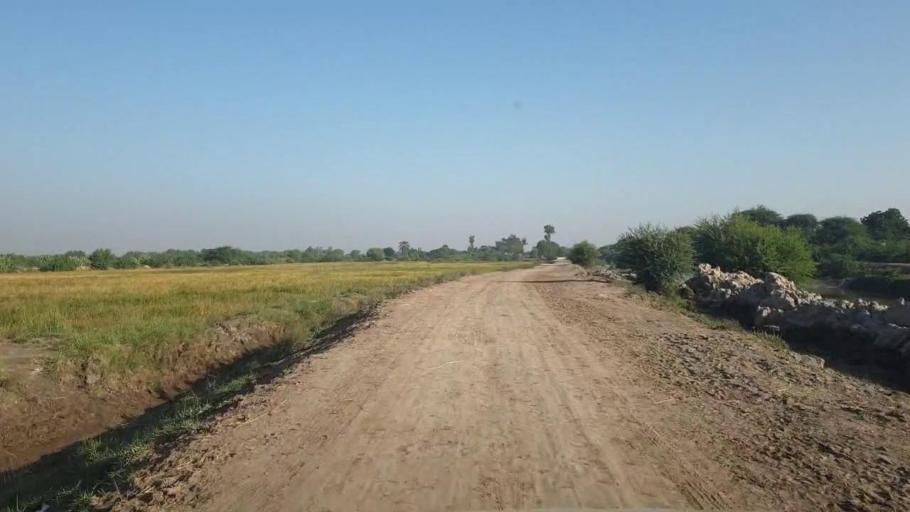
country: PK
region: Sindh
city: Badin
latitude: 24.6853
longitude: 68.8153
